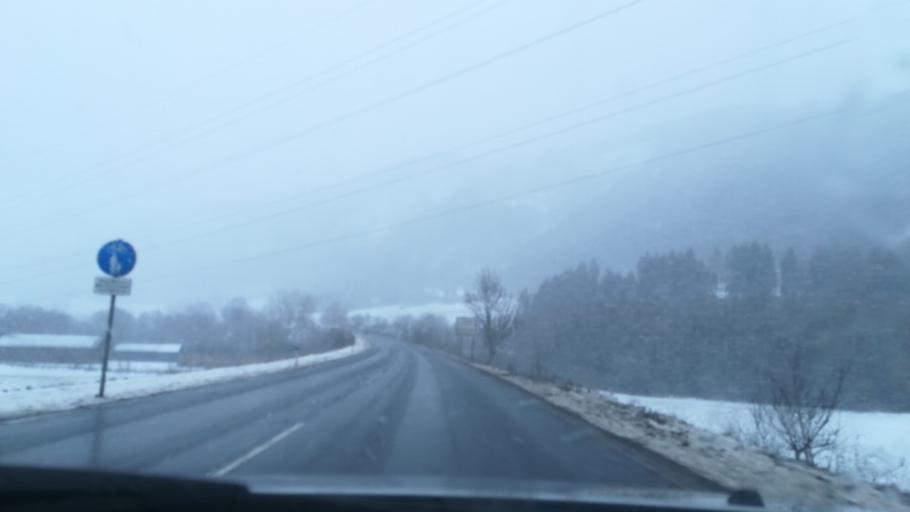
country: AT
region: Styria
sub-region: Politischer Bezirk Murtal
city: Sankt Peter ob Judenburg
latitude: 47.1874
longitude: 14.6001
